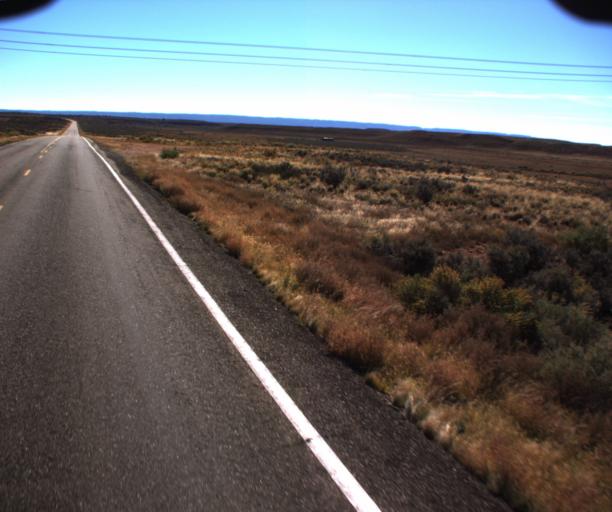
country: US
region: Arizona
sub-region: Coconino County
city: Fredonia
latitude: 36.9163
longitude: -112.4288
